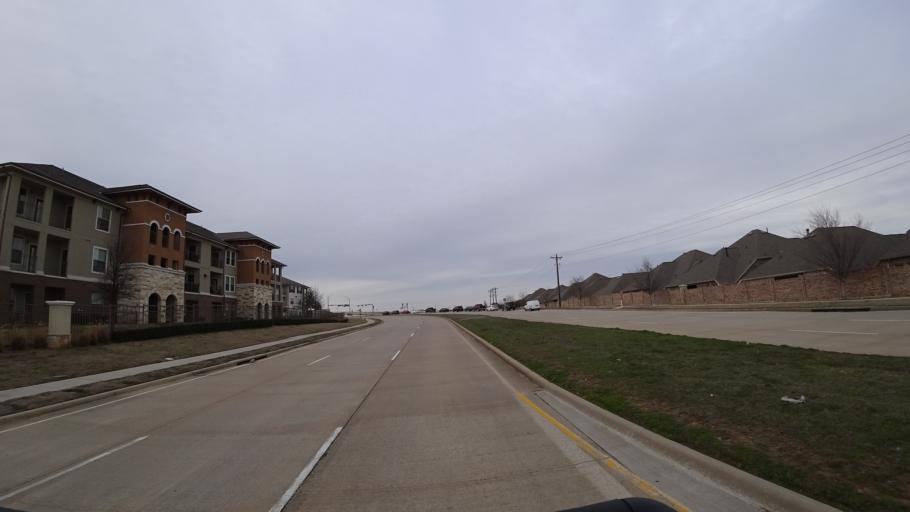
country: US
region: Texas
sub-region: Denton County
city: The Colony
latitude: 33.0489
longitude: -96.9187
